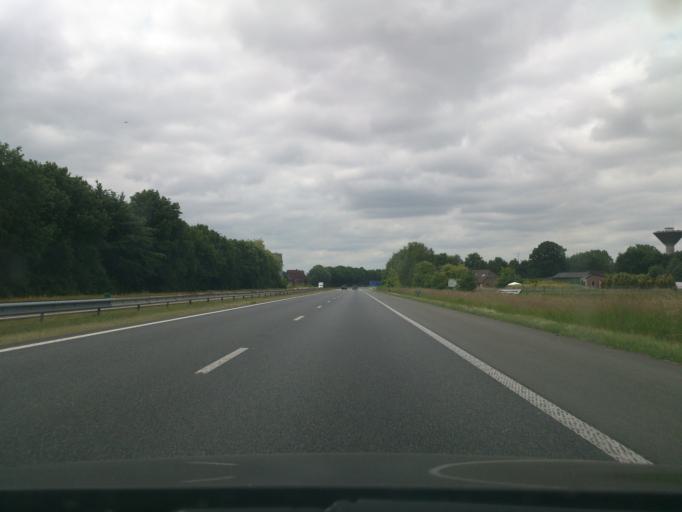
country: NL
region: Gelderland
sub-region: Gemeente Wijchen
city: Wijchen
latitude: 51.8170
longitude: 5.7108
